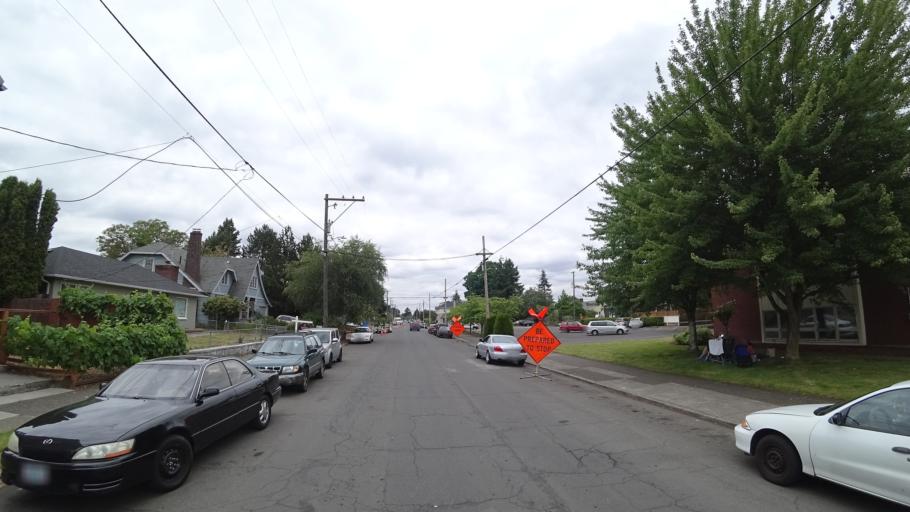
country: US
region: Oregon
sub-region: Multnomah County
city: Lents
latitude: 45.5204
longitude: -122.5815
